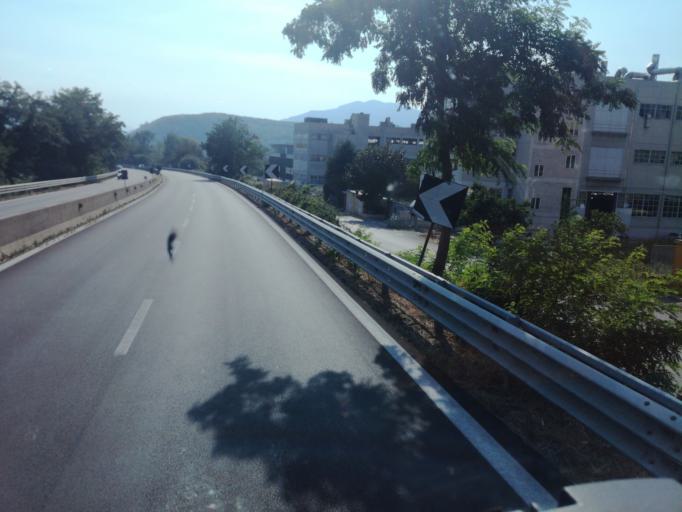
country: IT
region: Campania
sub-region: Provincia di Avellino
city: Solofra
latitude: 40.8331
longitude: 14.8231
